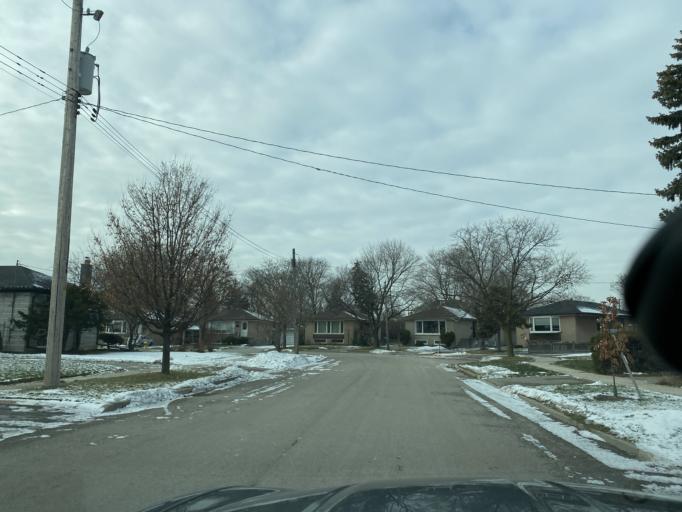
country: CA
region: Ontario
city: Etobicoke
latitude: 43.6607
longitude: -79.5786
